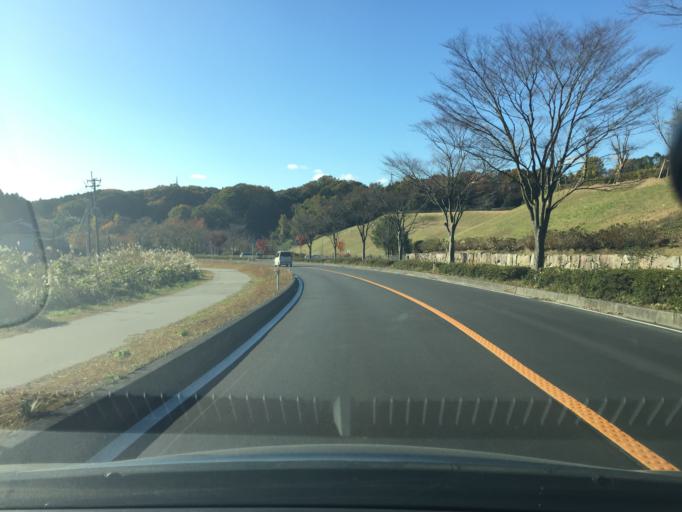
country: JP
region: Fukushima
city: Iwaki
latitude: 37.0129
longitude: 140.8650
